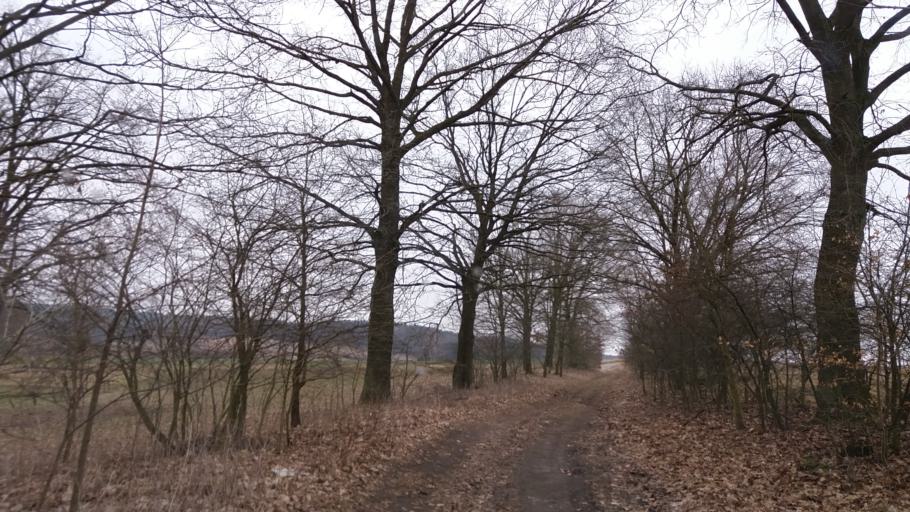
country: PL
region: West Pomeranian Voivodeship
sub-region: Powiat choszczenski
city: Recz
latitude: 53.1886
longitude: 15.5079
